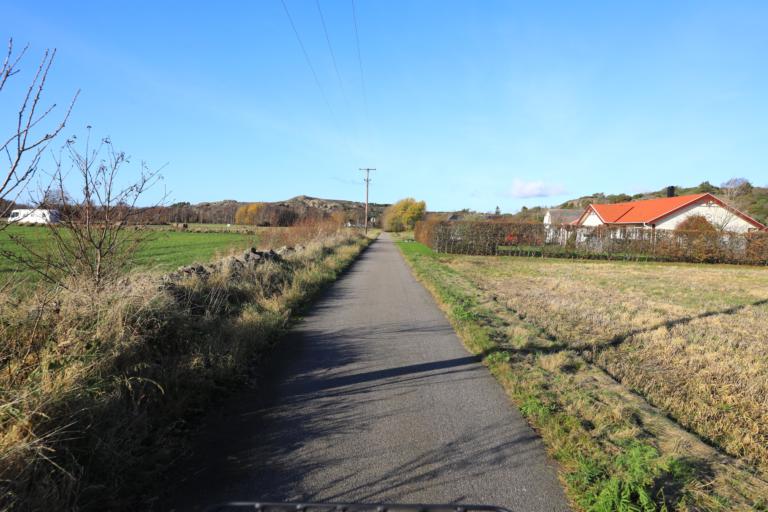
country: SE
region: Halland
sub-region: Varbergs Kommun
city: Varberg
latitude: 57.1527
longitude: 12.2431
